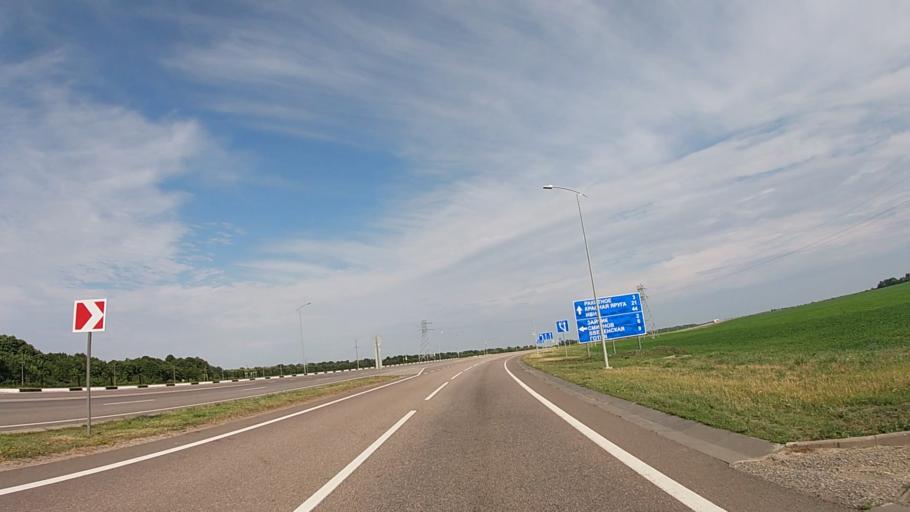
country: RU
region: Belgorod
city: Rakitnoye
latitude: 50.7905
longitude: 35.8694
